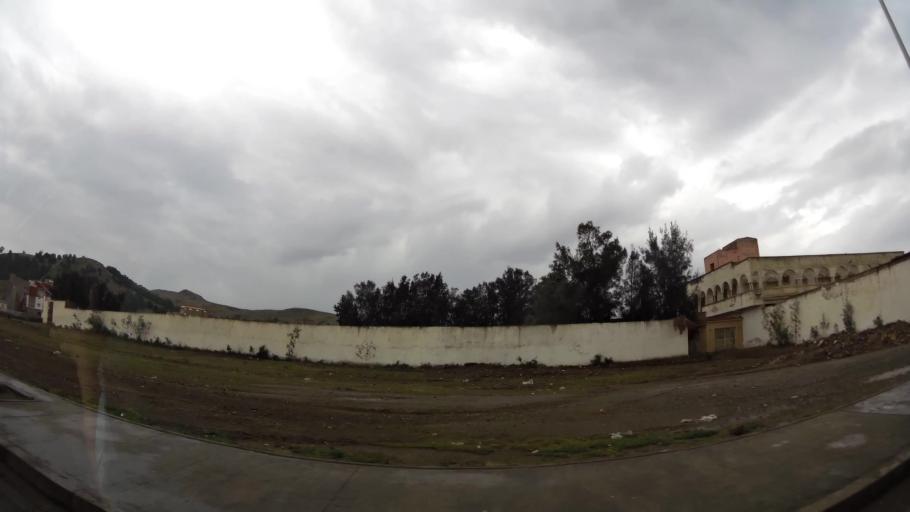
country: MA
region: Oriental
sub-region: Nador
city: Nador
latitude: 35.1495
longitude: -2.9793
